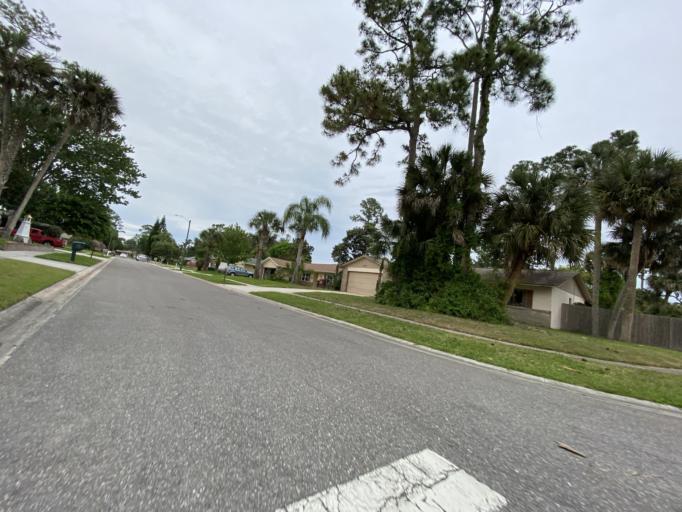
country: US
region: Florida
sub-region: Volusia County
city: Port Orange
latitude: 29.1509
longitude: -80.9999
